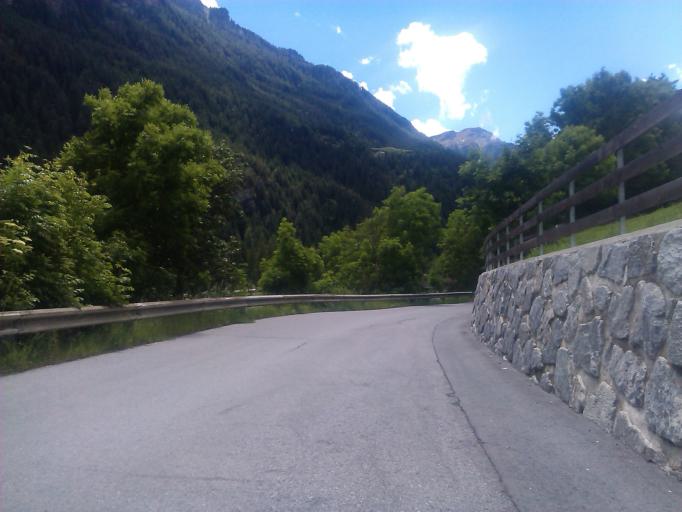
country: AT
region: Tyrol
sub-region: Politischer Bezirk Landeck
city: Serfaus
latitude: 47.0037
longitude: 10.5902
